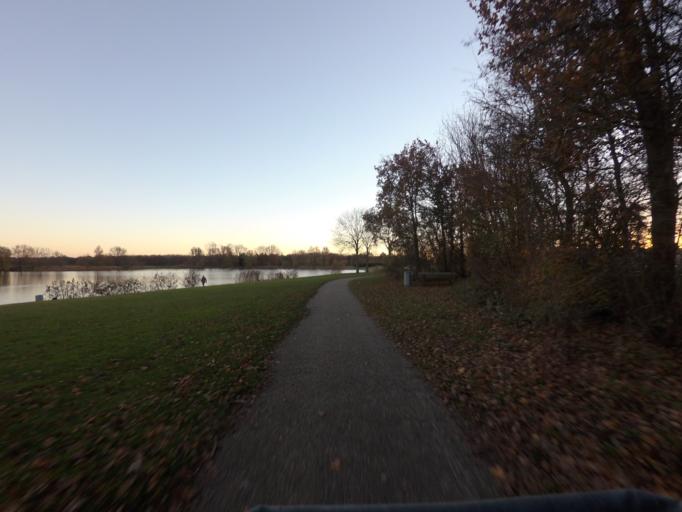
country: NL
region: Utrecht
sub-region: Gemeente Nieuwegein
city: Nieuwegein
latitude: 52.0739
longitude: 5.0561
